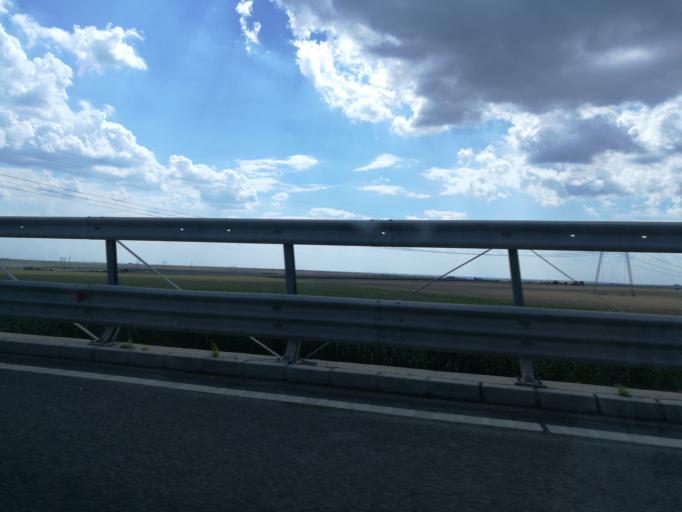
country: RO
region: Constanta
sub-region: Comuna Ovidiu
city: Ovidiu
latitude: 44.2276
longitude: 28.5503
